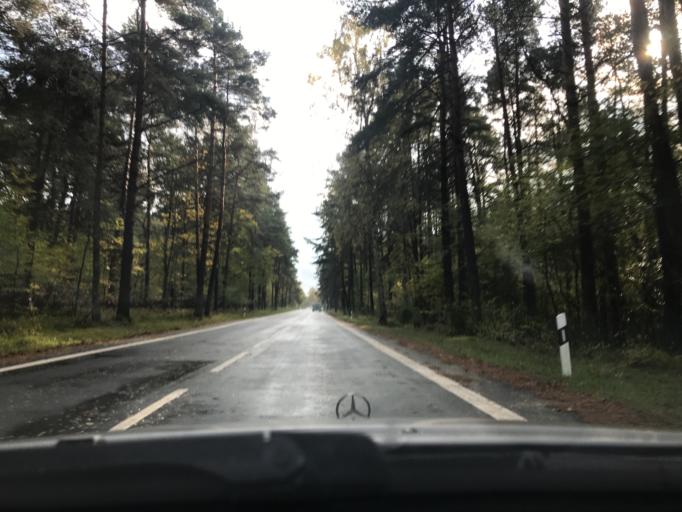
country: DE
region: Mecklenburg-Vorpommern
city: Karlshagen
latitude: 54.1412
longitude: 13.8230
